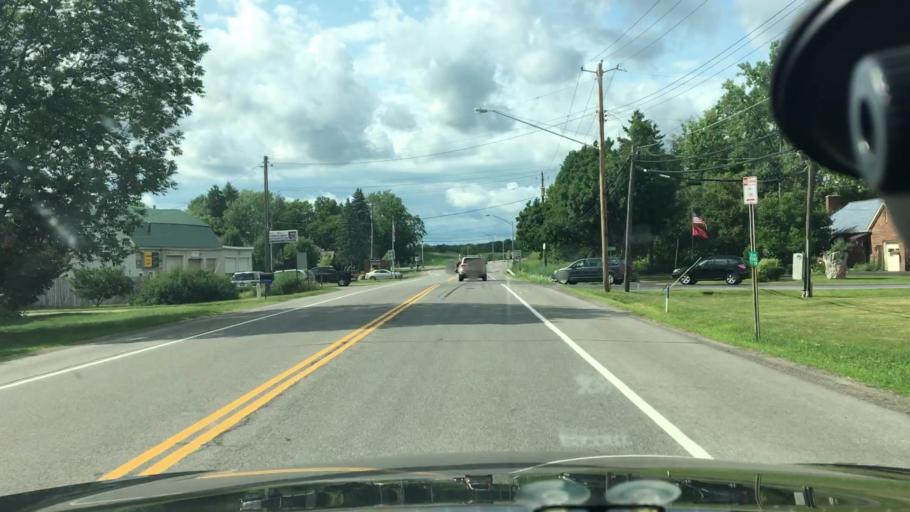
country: US
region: New York
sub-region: Erie County
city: North Boston
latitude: 42.6914
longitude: -78.7826
